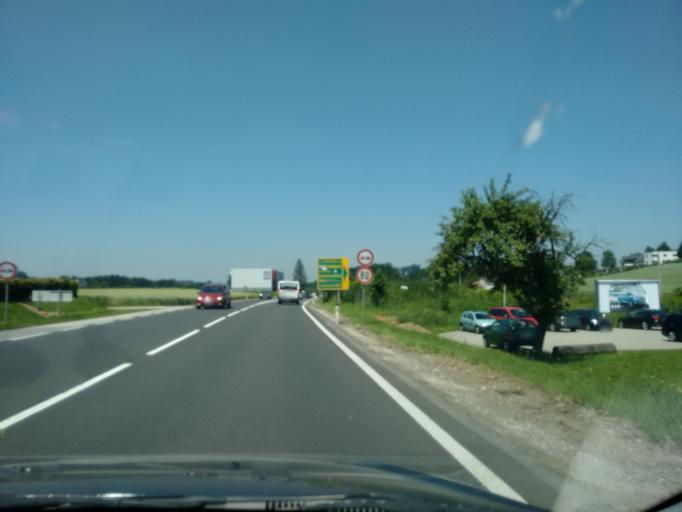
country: AT
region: Upper Austria
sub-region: Politischer Bezirk Gmunden
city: Altmunster
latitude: 47.9391
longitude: 13.7575
